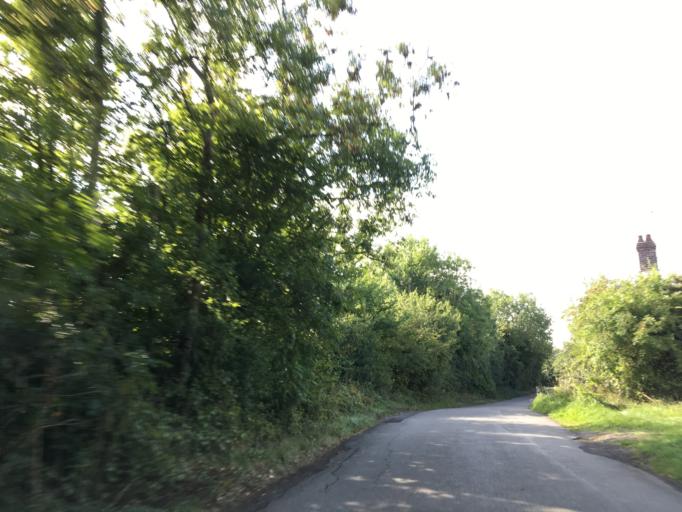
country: GB
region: England
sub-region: South Gloucestershire
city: Horton
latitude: 51.5278
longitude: -2.3592
